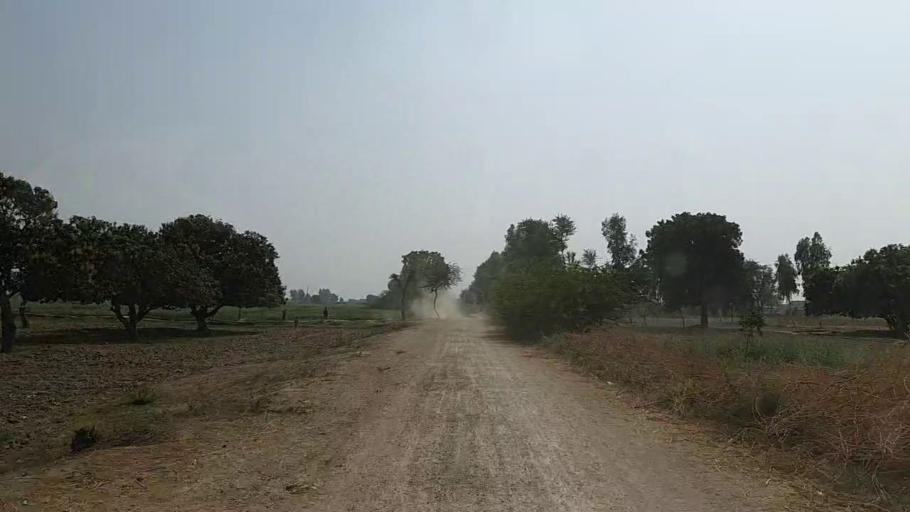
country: PK
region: Sindh
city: Naukot
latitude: 24.7815
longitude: 69.3514
